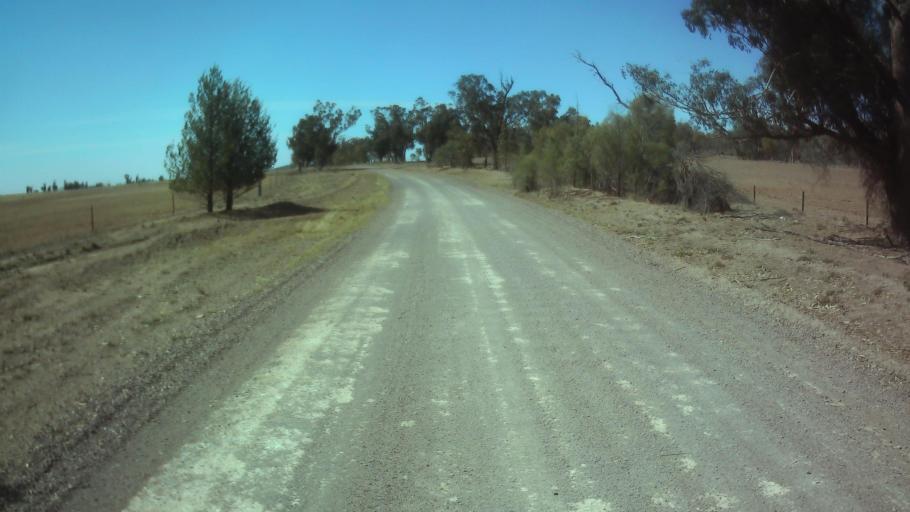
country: AU
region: New South Wales
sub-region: Forbes
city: Forbes
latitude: -33.7156
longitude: 147.7469
